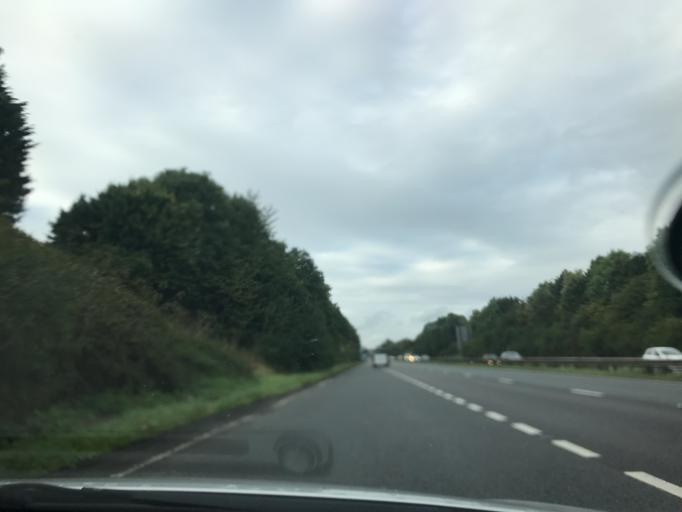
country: GB
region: England
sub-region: Cheshire West and Chester
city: Guilden Sutton
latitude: 53.1982
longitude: -2.8444
